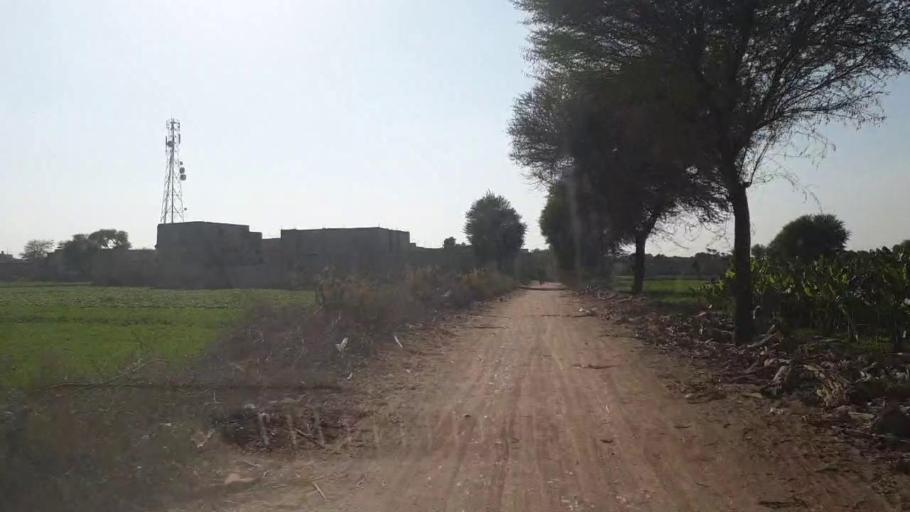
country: PK
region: Sindh
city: Tando Allahyar
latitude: 25.4269
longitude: 68.6584
